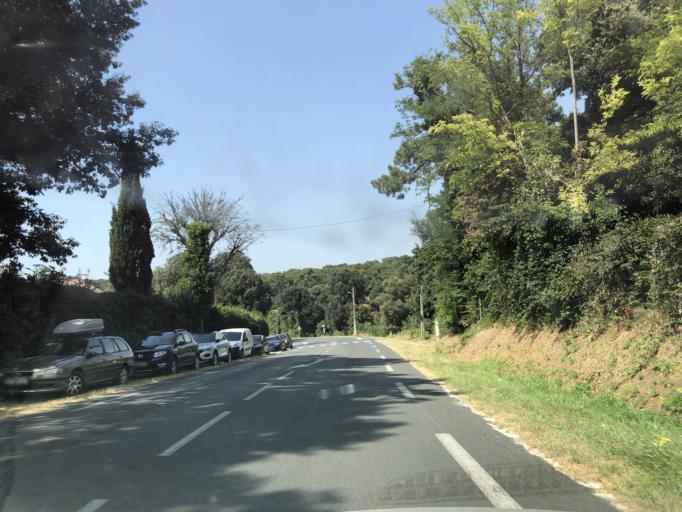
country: FR
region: Poitou-Charentes
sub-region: Departement de la Charente-Maritime
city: Meschers-sur-Gironde
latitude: 45.5638
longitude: -0.9695
